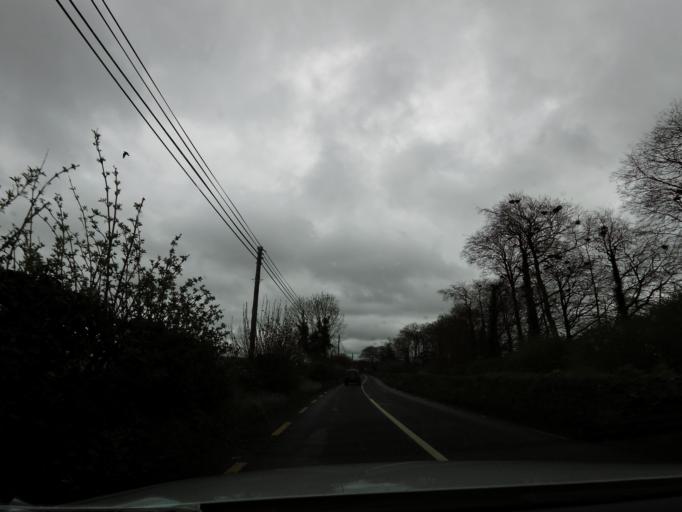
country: IE
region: Leinster
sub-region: Laois
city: Rathdowney
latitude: 52.7218
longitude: -7.5190
